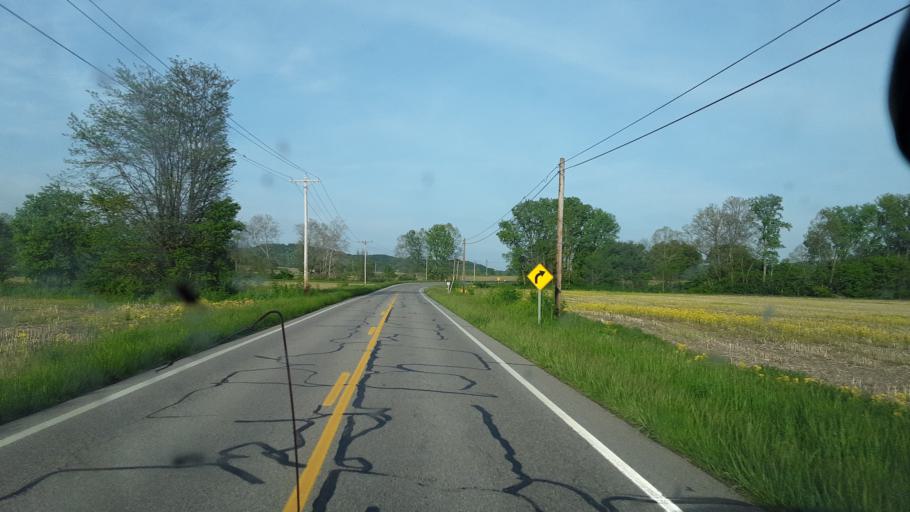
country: US
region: Ohio
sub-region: Ross County
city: Kingston
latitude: 39.4973
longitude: -82.7058
